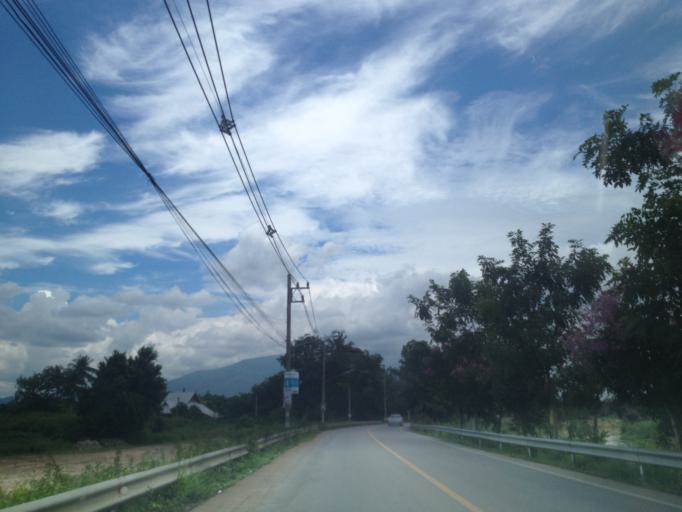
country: TH
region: Chiang Mai
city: Saraphi
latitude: 18.7271
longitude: 98.9859
